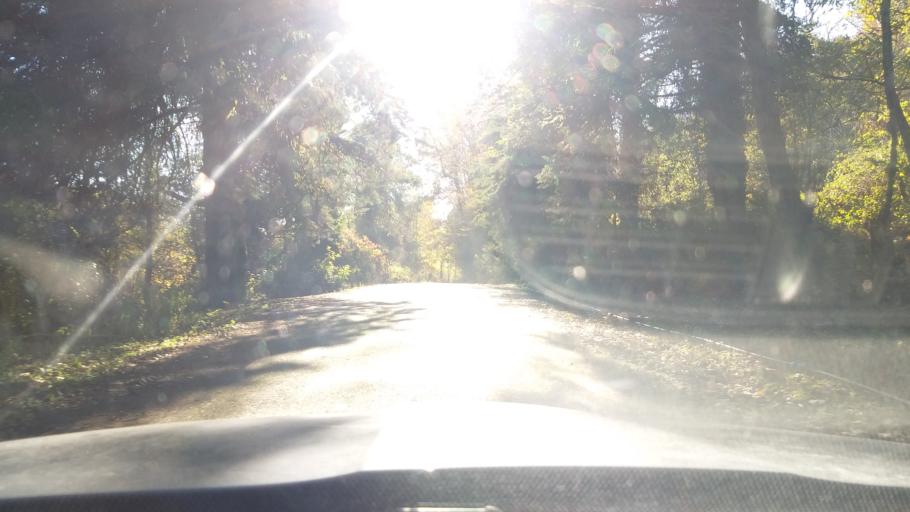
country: GE
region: Abkhazia
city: Bich'vinta
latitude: 43.1845
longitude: 40.4542
